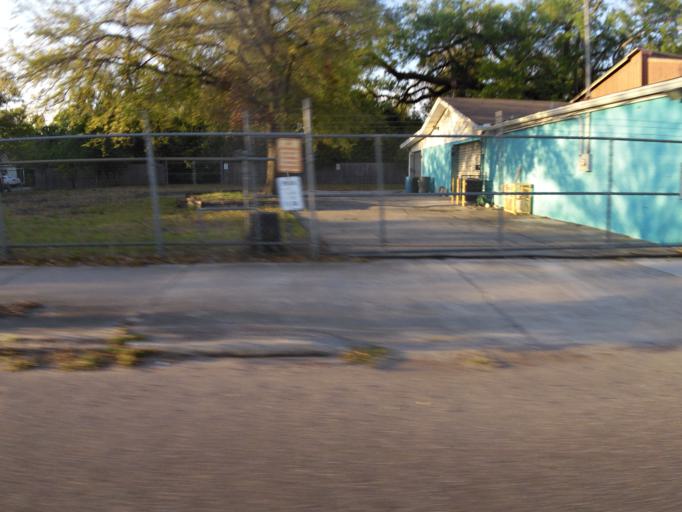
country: US
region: Florida
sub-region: Duval County
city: Jacksonville
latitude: 30.3231
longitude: -81.6939
